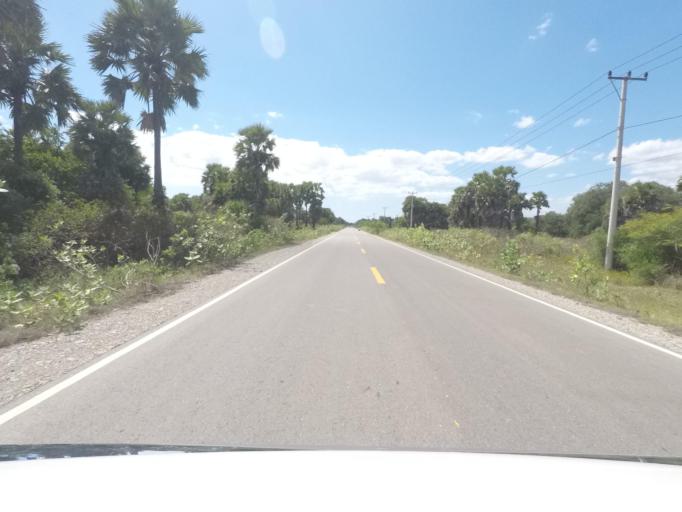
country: TL
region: Lautem
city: Lospalos
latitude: -8.3864
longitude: 126.8551
